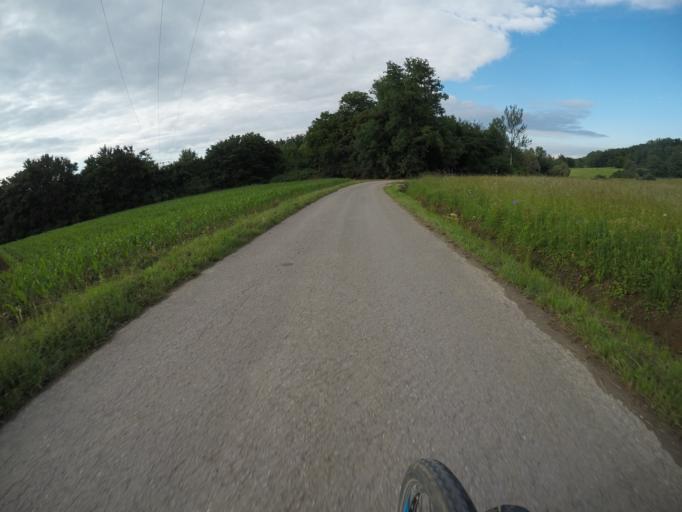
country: DE
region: Baden-Wuerttemberg
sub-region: Regierungsbezirk Stuttgart
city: Schlaitdorf
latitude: 48.6119
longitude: 9.2132
